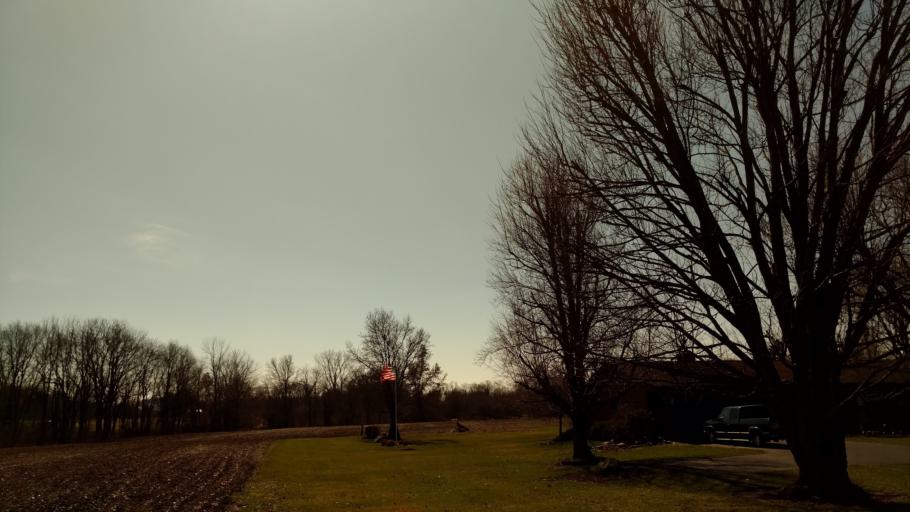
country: US
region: Ohio
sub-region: Marion County
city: Prospect
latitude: 40.4913
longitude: -83.1731
